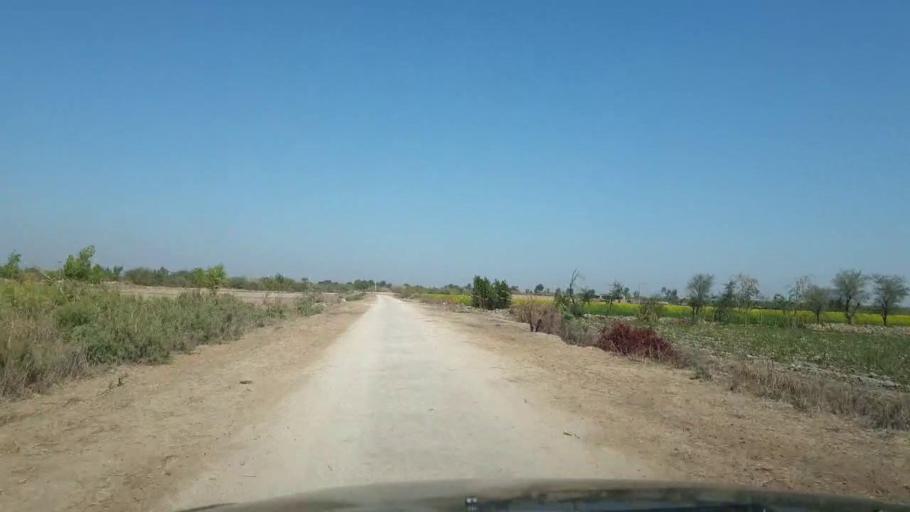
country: PK
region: Sindh
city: Mirpur Khas
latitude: 25.5949
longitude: 69.0683
